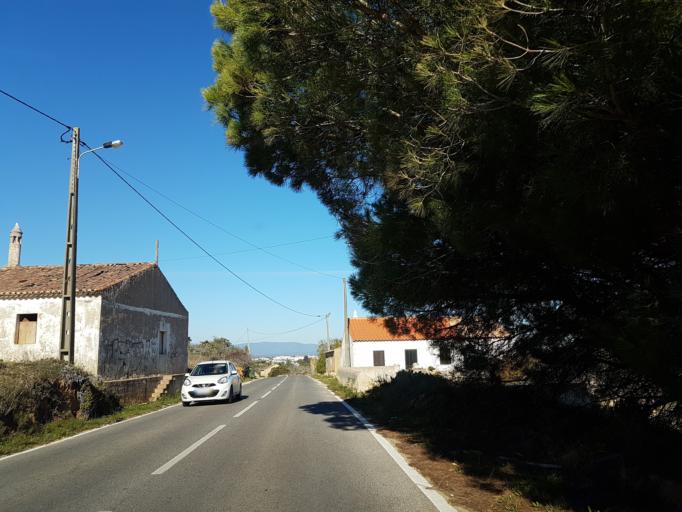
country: PT
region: Faro
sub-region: Lagoa
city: Carvoeiro
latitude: 37.1029
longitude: -8.4443
